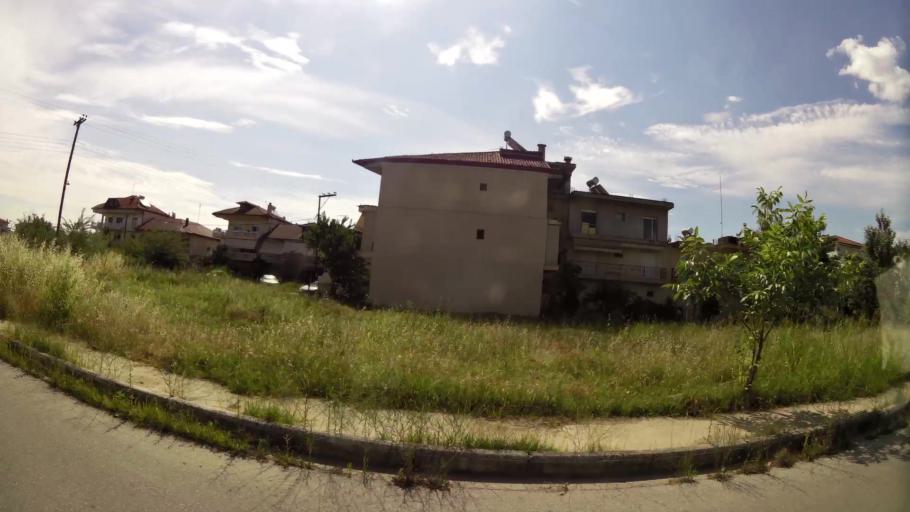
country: GR
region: Central Macedonia
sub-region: Nomos Pierias
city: Katerini
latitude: 40.2781
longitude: 22.4905
